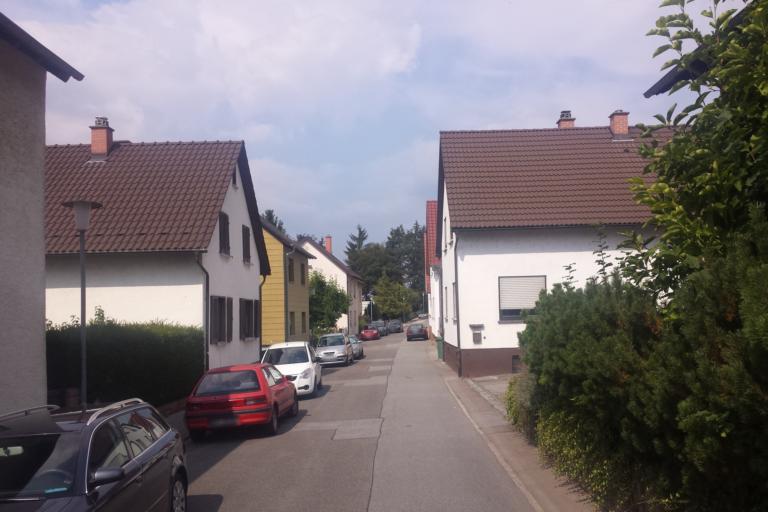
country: DE
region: Baden-Wuerttemberg
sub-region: Karlsruhe Region
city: Hemsbach
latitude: 49.5810
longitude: 8.6596
